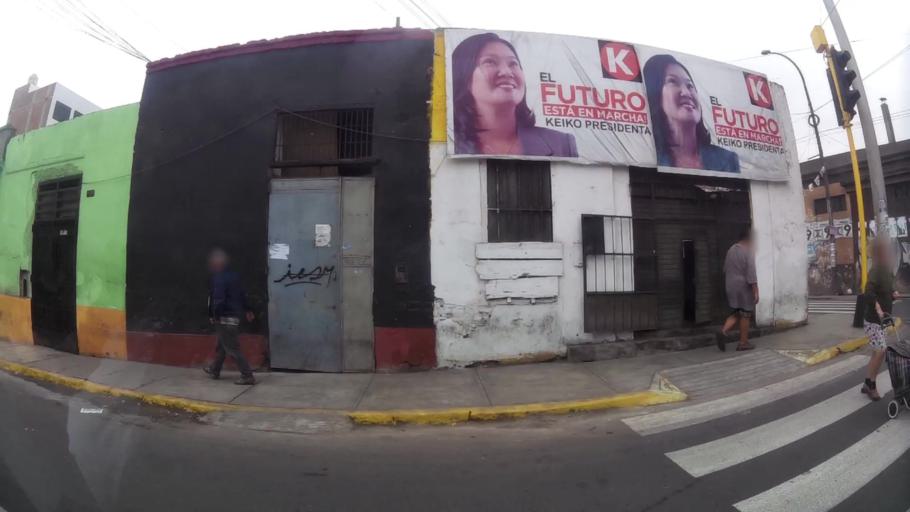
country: PE
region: Lima
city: Lima
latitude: -12.0509
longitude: -77.0194
